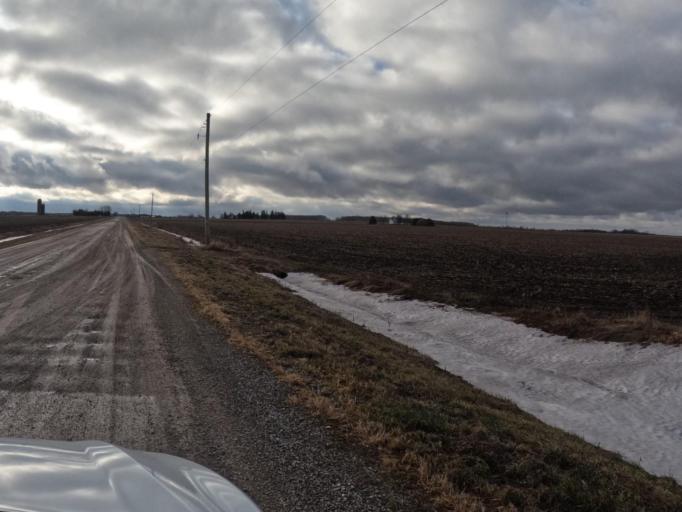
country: CA
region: Ontario
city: Shelburne
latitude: 43.8896
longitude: -80.3600
